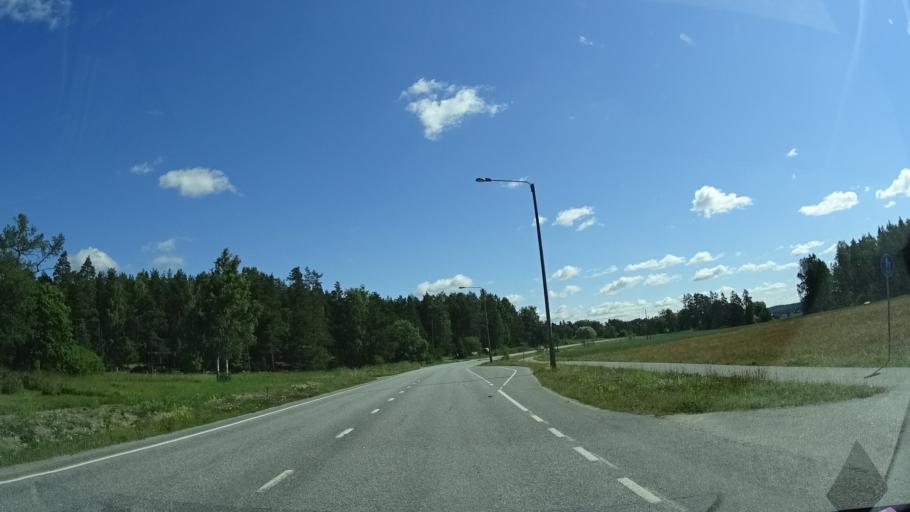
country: FI
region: Varsinais-Suomi
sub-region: Turku
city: Lemu
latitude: 60.5703
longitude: 21.9831
